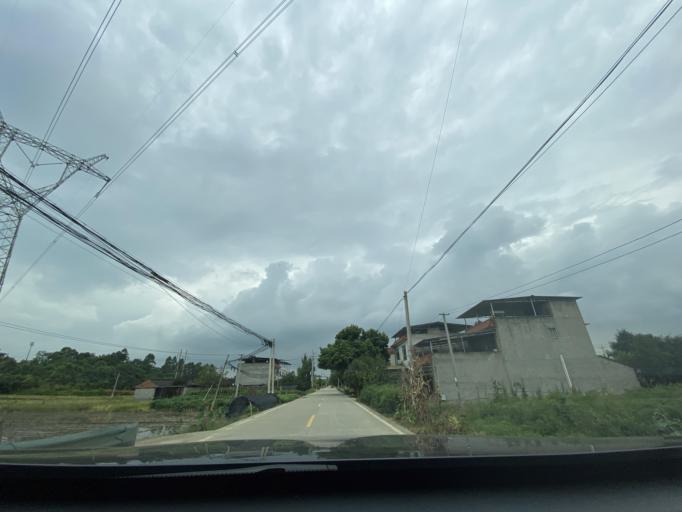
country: CN
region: Sichuan
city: Wujin
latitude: 30.3820
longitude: 103.9678
